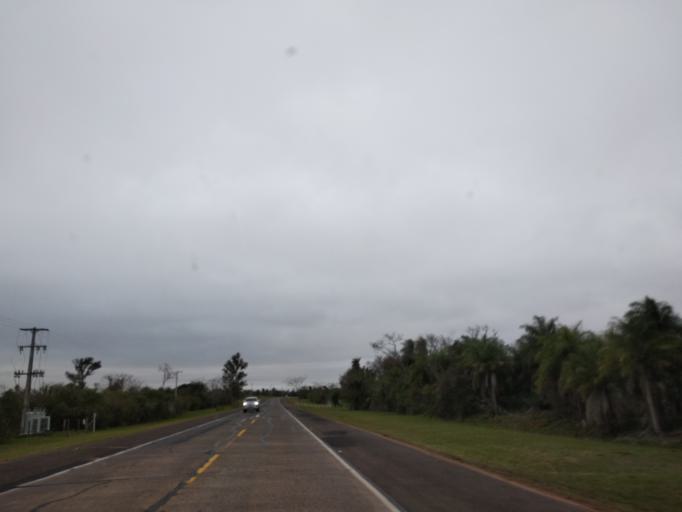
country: PY
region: Misiones
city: Santa Maria
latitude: -26.8689
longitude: -57.1110
